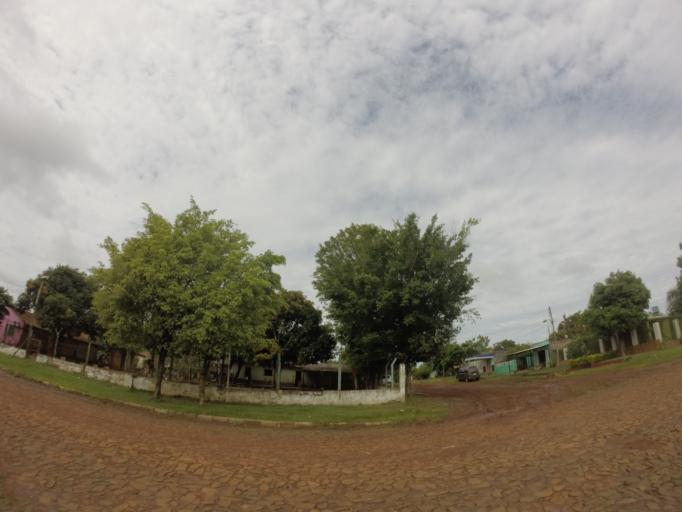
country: PY
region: Alto Parana
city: Ciudad del Este
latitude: -25.4025
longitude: -54.6532
